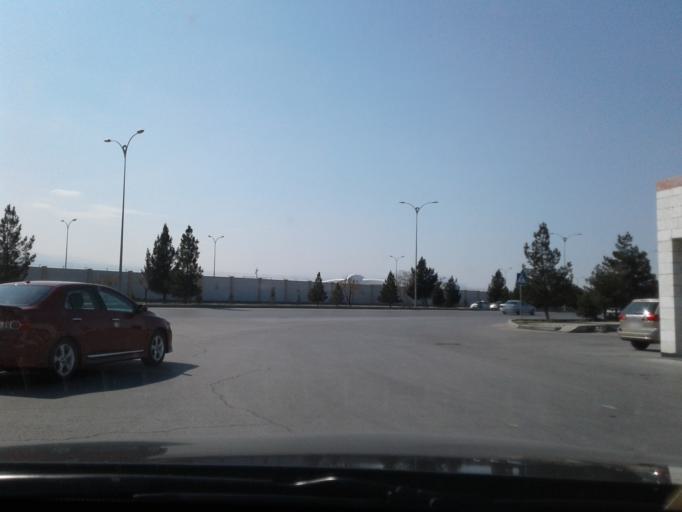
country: TM
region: Ahal
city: Ashgabat
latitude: 37.9818
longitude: 58.3883
